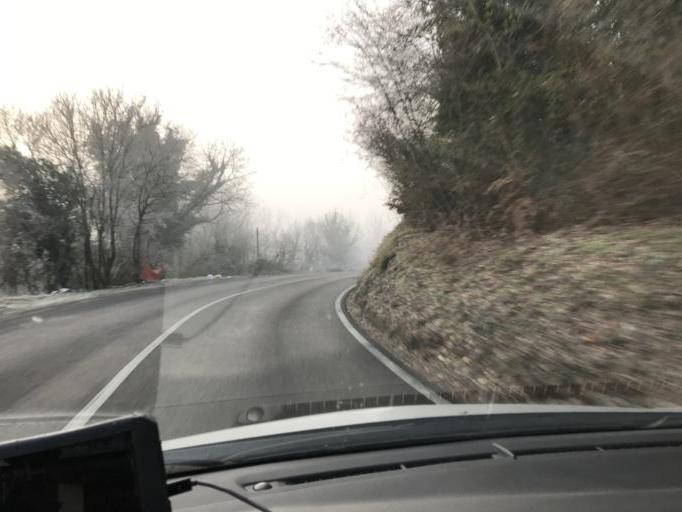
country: IT
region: Latium
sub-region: Provincia di Rieti
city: Colli sul Velino
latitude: 42.5169
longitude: 12.7379
